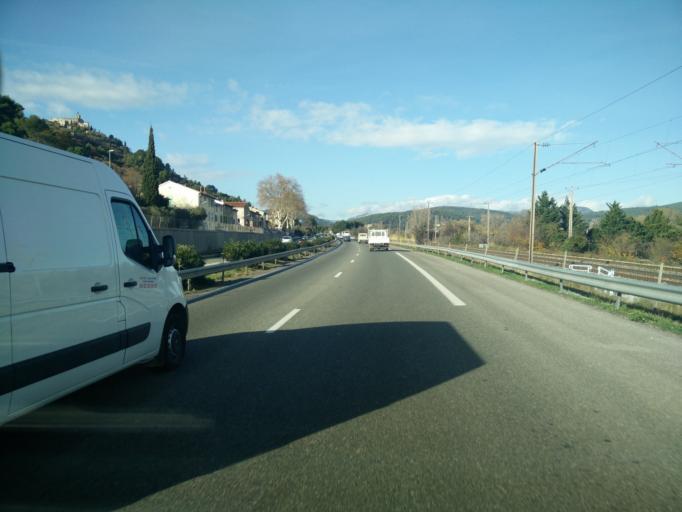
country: FR
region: Provence-Alpes-Cote d'Azur
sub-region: Departement du Var
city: Sollies-Ville
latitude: 43.1779
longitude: 6.0477
